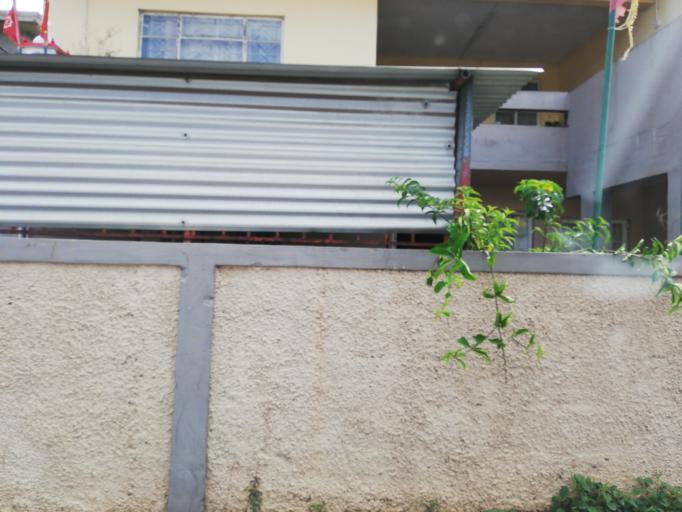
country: MU
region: Black River
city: Petite Riviere
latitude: -20.2181
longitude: 57.4647
